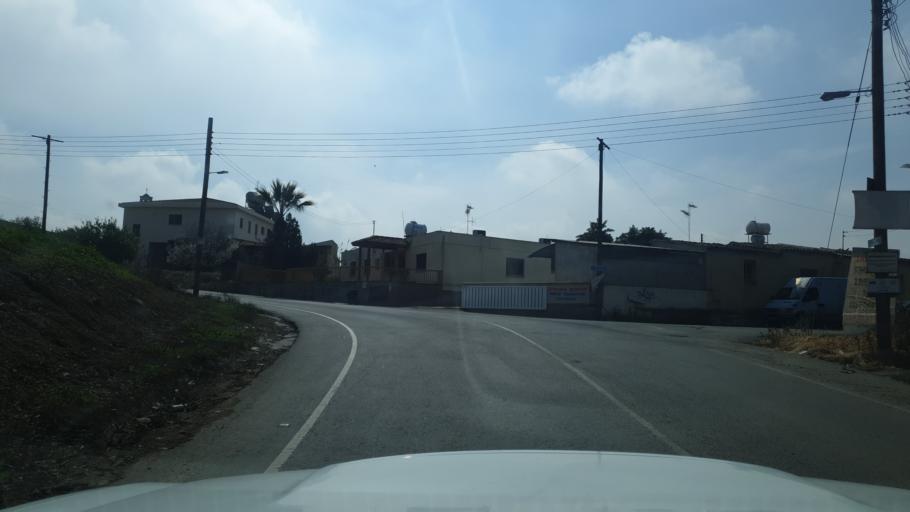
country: CY
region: Lefkosia
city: Kato Deftera
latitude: 35.0874
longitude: 33.2771
